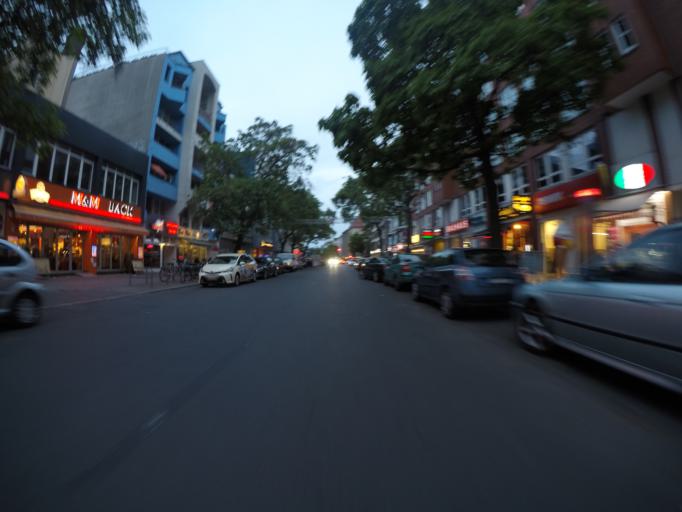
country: DE
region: Berlin
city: Charlottenburg-Nord
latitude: 52.5128
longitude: 13.3050
